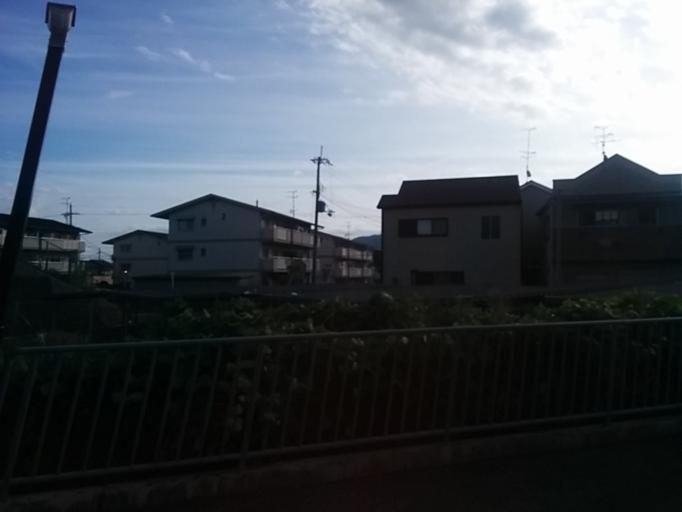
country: JP
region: Kyoto
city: Tanabe
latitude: 34.8088
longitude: 135.7783
